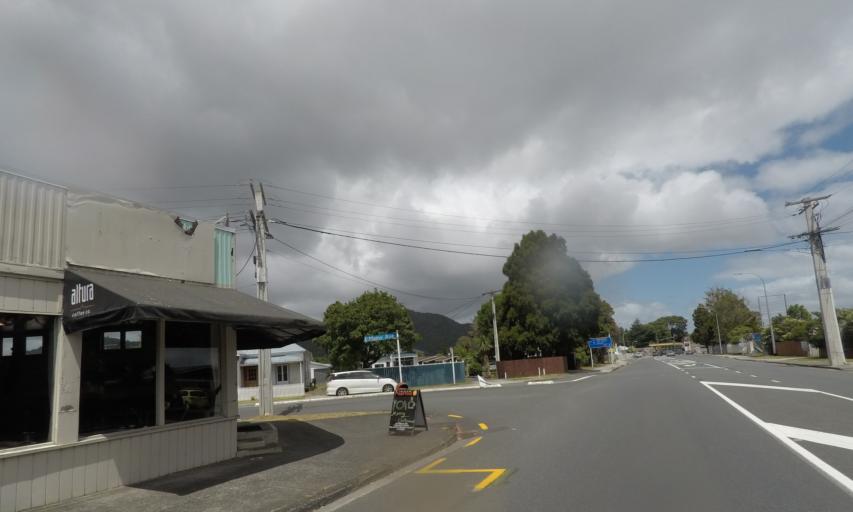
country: NZ
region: Northland
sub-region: Whangarei
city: Whangarei
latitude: -35.7069
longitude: 174.3205
